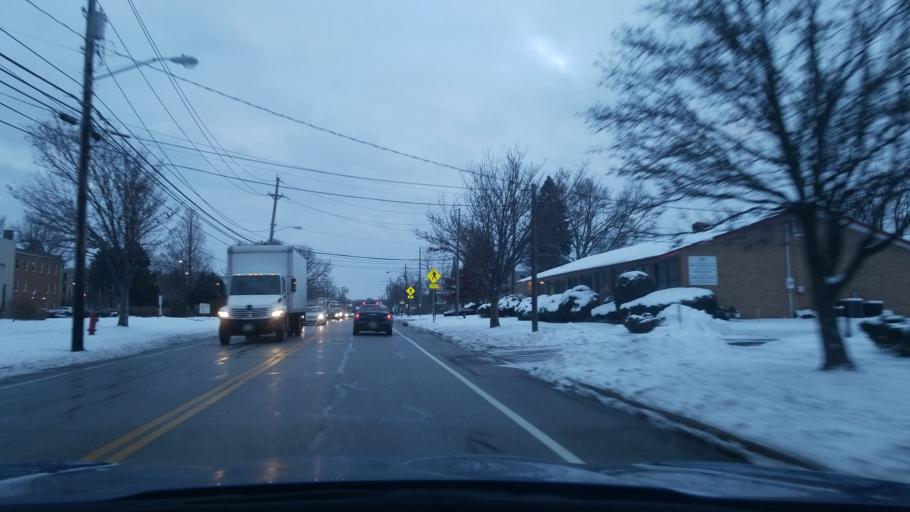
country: US
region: Ohio
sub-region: Cuyahoga County
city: Berea
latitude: 41.3753
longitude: -81.8531
